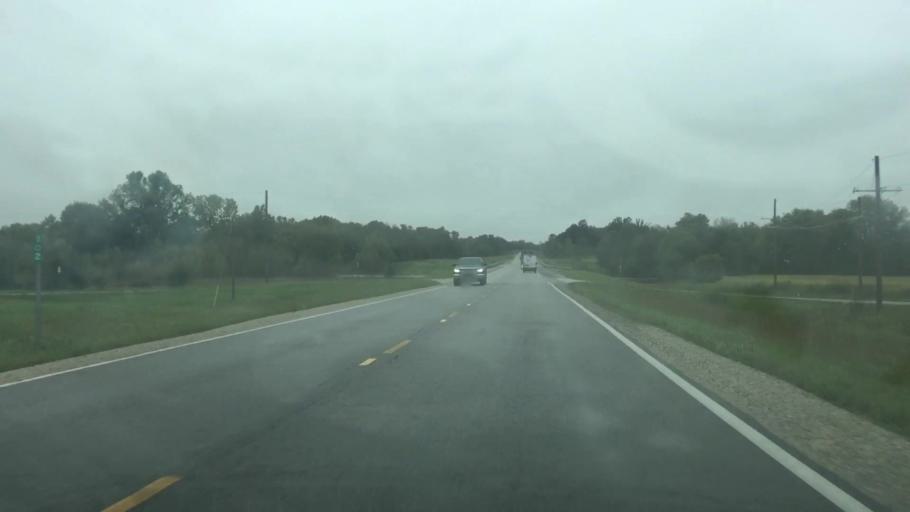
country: US
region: Kansas
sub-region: Anderson County
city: Garnett
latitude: 38.2132
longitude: -95.2488
